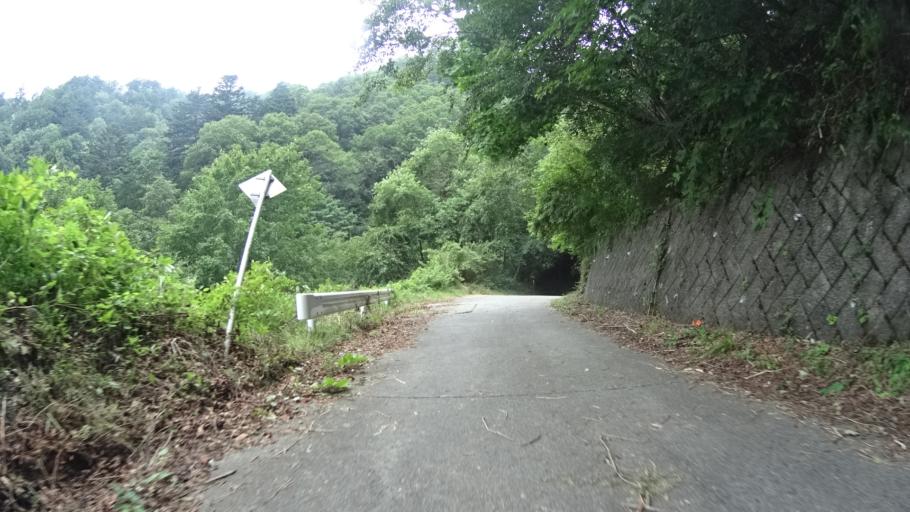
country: JP
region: Yamanashi
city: Kofu-shi
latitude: 35.8277
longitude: 138.5839
